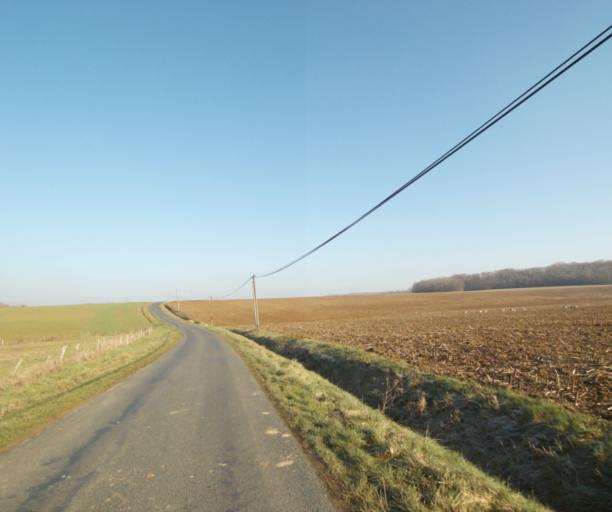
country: FR
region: Champagne-Ardenne
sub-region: Departement de la Haute-Marne
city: Bienville
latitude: 48.5307
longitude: 5.0059
